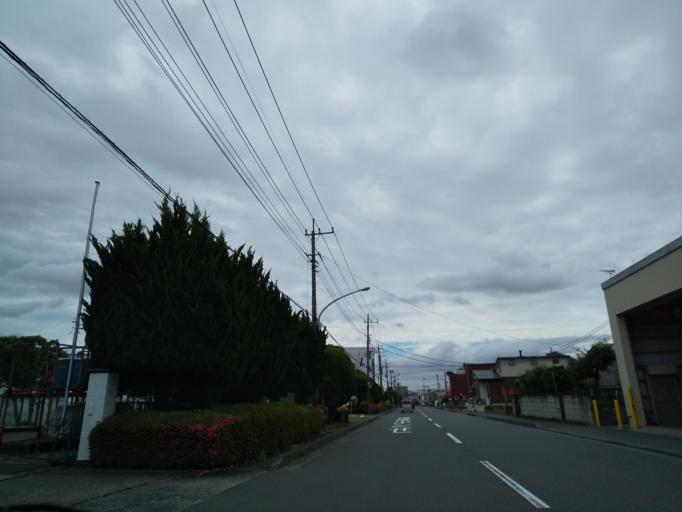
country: JP
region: Kanagawa
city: Zama
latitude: 35.5219
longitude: 139.3388
